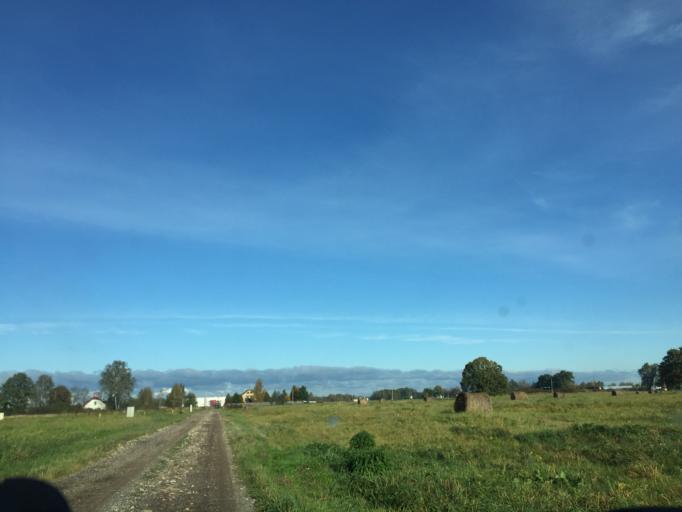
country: LV
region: Adazi
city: Adazi
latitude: 57.0905
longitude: 24.3088
